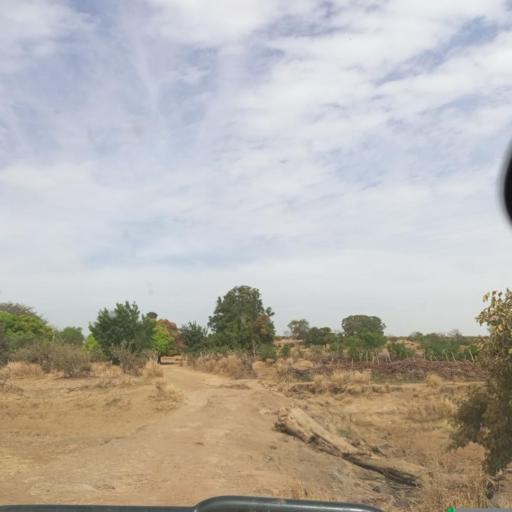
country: ML
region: Koulikoro
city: Koulikoro
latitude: 13.1670
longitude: -7.7290
